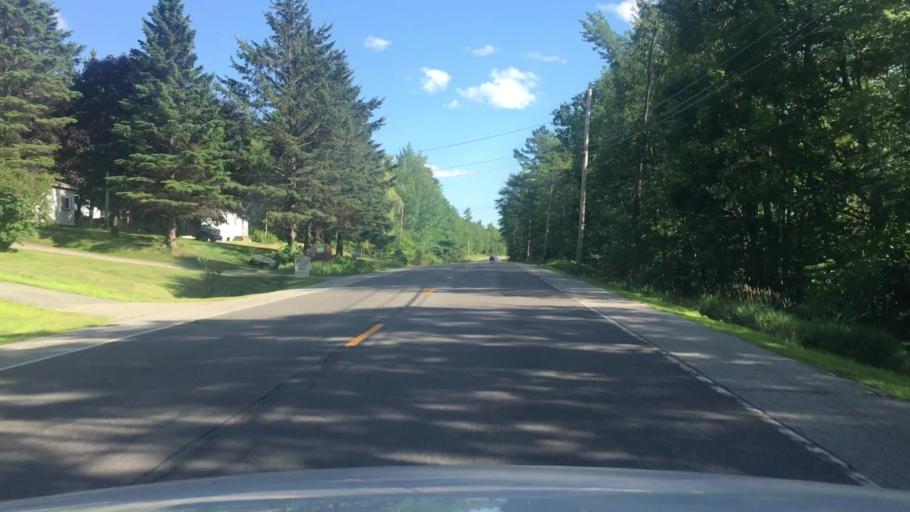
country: US
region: Maine
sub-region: Franklin County
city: Jay
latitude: 44.5426
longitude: -70.2362
